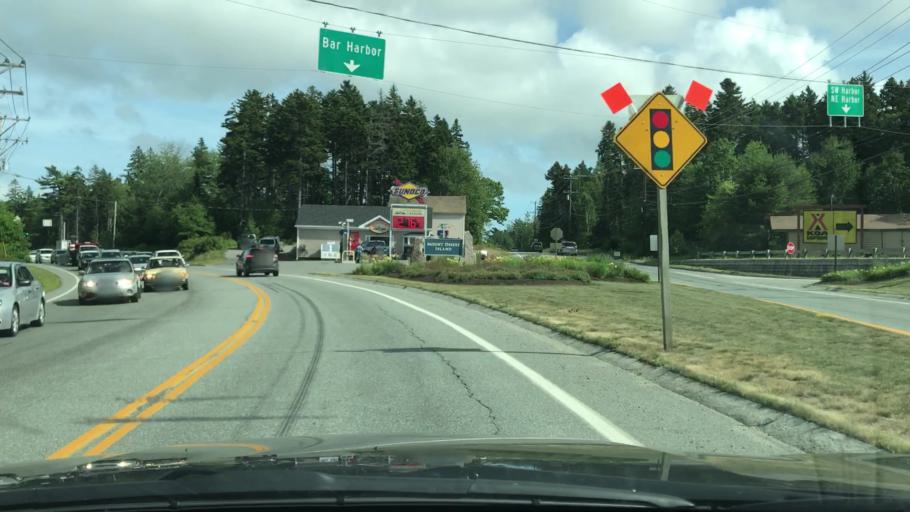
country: US
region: Maine
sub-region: Hancock County
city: Trenton
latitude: 44.4217
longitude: -68.3638
